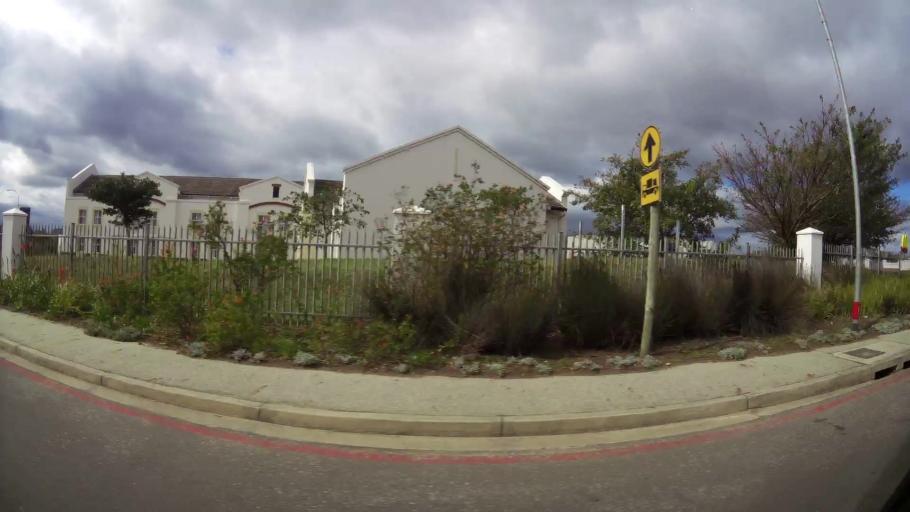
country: ZA
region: Western Cape
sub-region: Eden District Municipality
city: George
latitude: -33.9847
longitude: 22.5020
